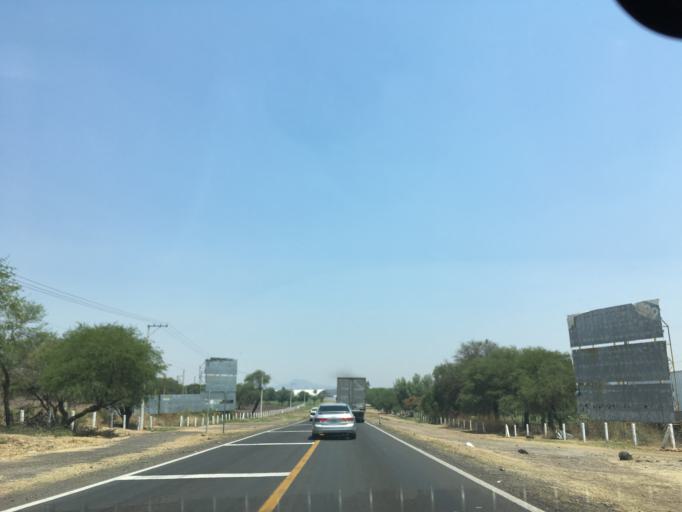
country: MX
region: Michoacan
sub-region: Cuitzeo
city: Cuamio
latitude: 20.0619
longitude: -101.1515
